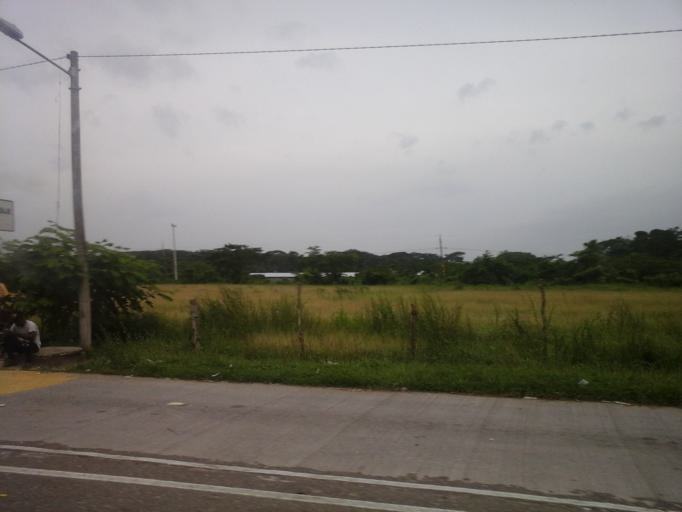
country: CO
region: Bolivar
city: San Pablo
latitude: 10.1364
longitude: -75.2685
